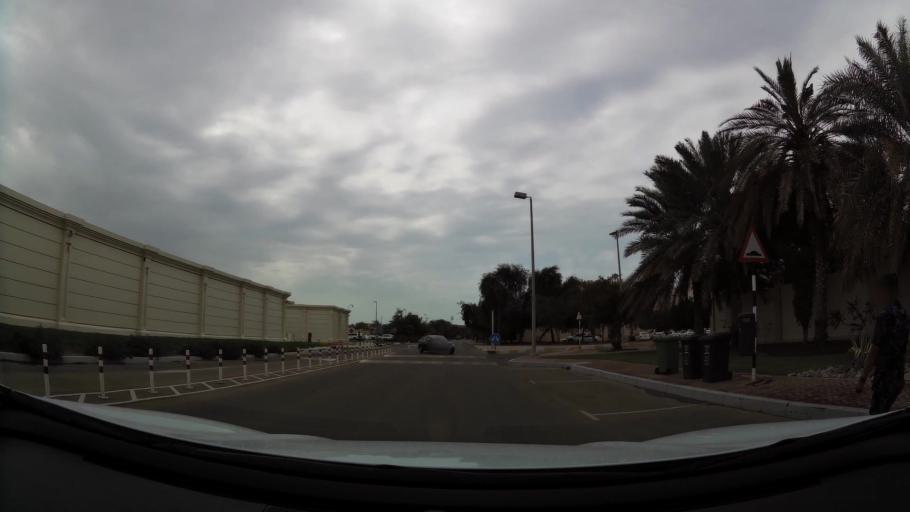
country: AE
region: Abu Dhabi
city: Abu Dhabi
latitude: 24.4239
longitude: 54.4232
